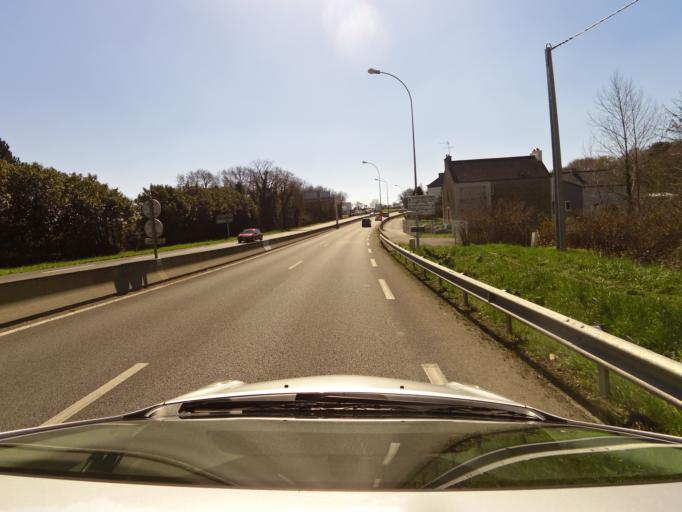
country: FR
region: Brittany
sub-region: Departement du Morbihan
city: Larmor-Plage
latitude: 47.7236
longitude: -3.3825
